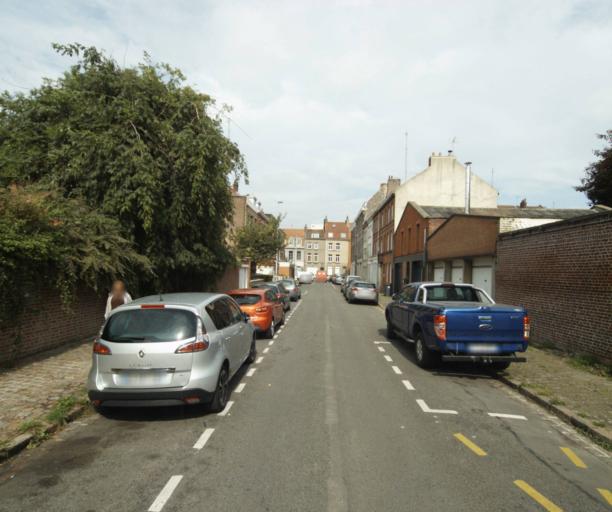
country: FR
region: Nord-Pas-de-Calais
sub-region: Departement du Nord
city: Lille
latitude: 50.6246
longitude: 3.0429
